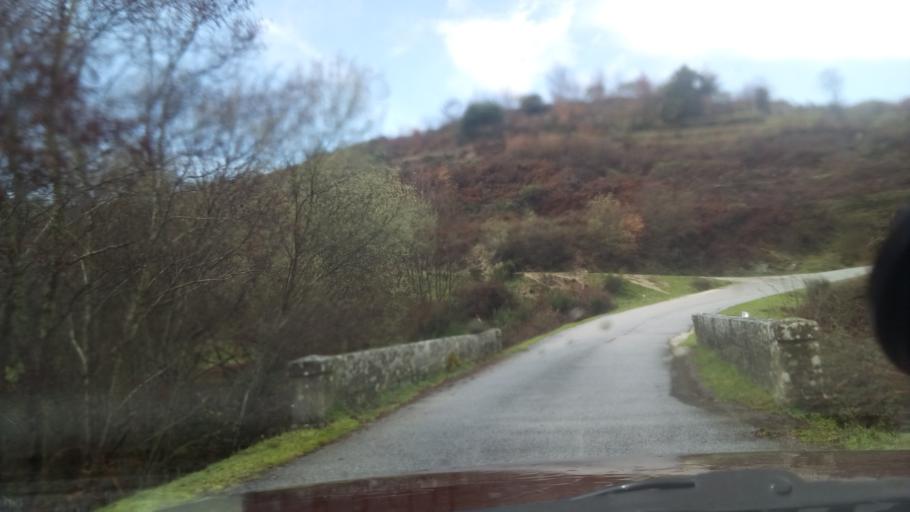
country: PT
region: Guarda
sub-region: Fornos de Algodres
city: Fornos de Algodres
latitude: 40.5475
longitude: -7.4804
